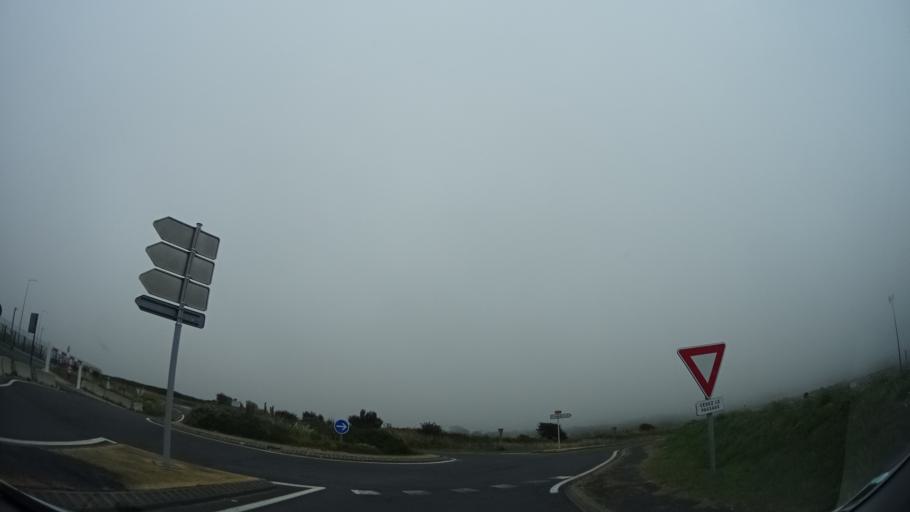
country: FR
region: Lower Normandy
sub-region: Departement de la Manche
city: Flamanville
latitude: 49.5320
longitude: -1.8802
